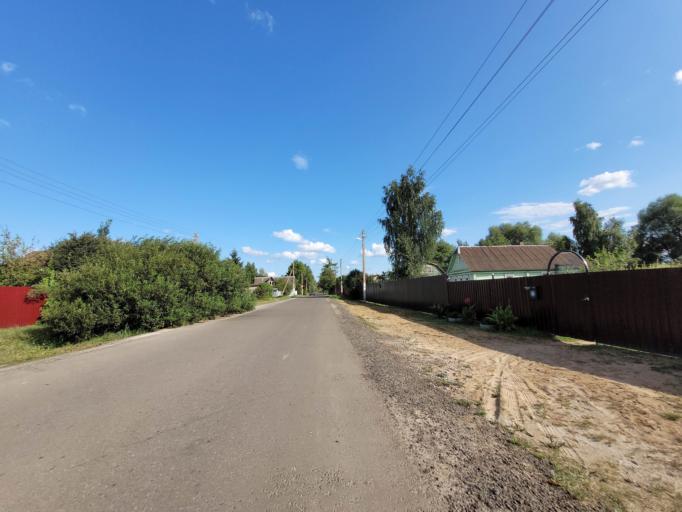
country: RU
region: Moskovskaya
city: Konobeyevo
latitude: 55.4080
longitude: 38.7018
